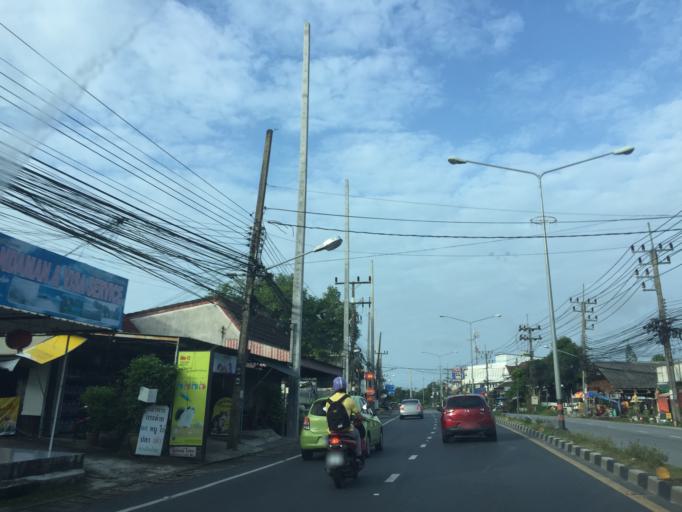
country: TH
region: Phuket
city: Mueang Phuket
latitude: 7.8654
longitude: 98.3713
